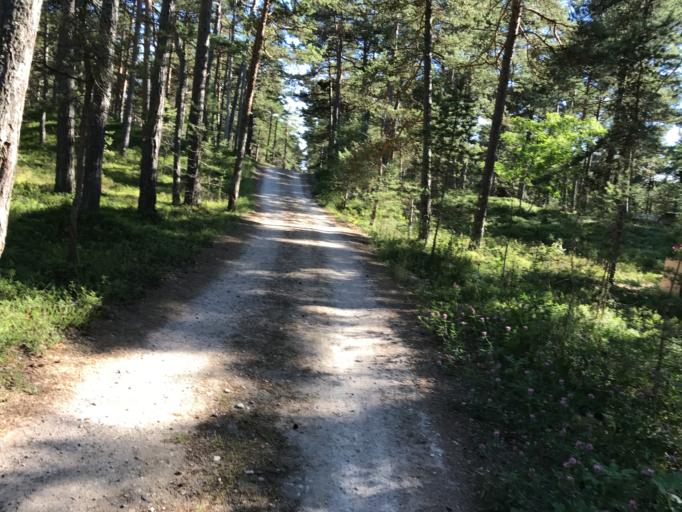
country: EE
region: Harju
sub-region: Paldiski linn
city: Paldiski
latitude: 59.3847
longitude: 24.2242
